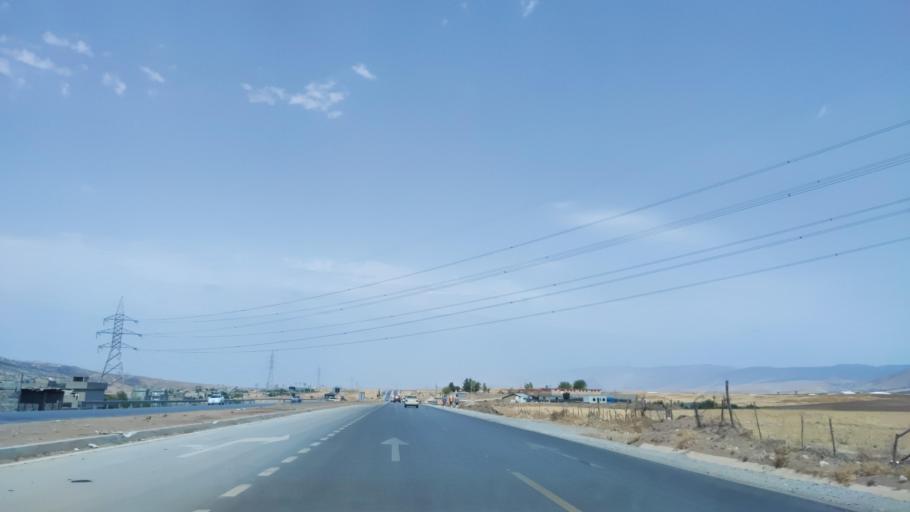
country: IQ
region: Arbil
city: Shaqlawah
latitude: 36.5052
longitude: 44.3518
